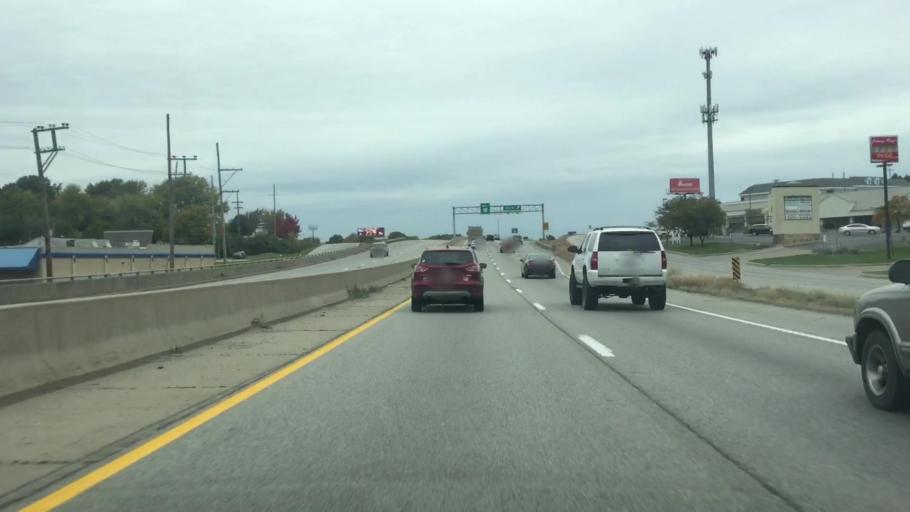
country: US
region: Missouri
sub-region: Jackson County
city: Lees Summit
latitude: 38.9086
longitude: -94.3894
